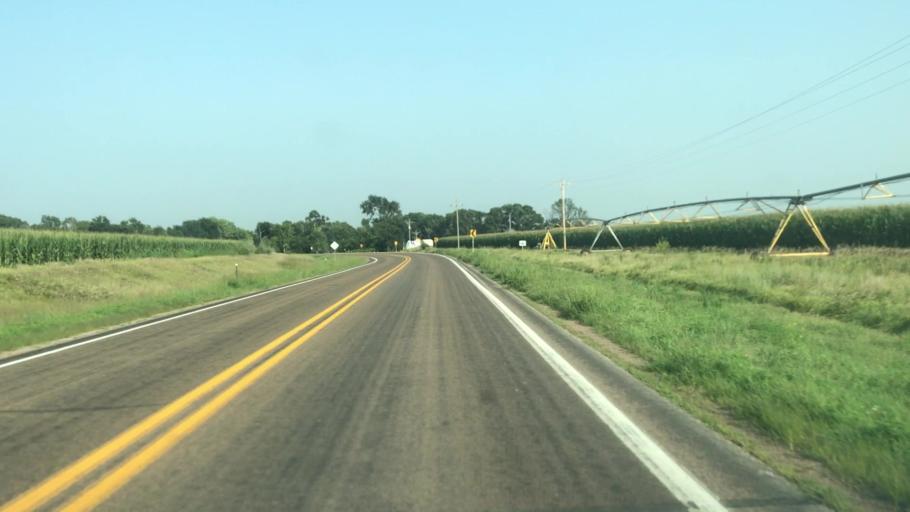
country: US
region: Nebraska
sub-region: Buffalo County
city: Ravenna
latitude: 41.0750
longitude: -98.7273
